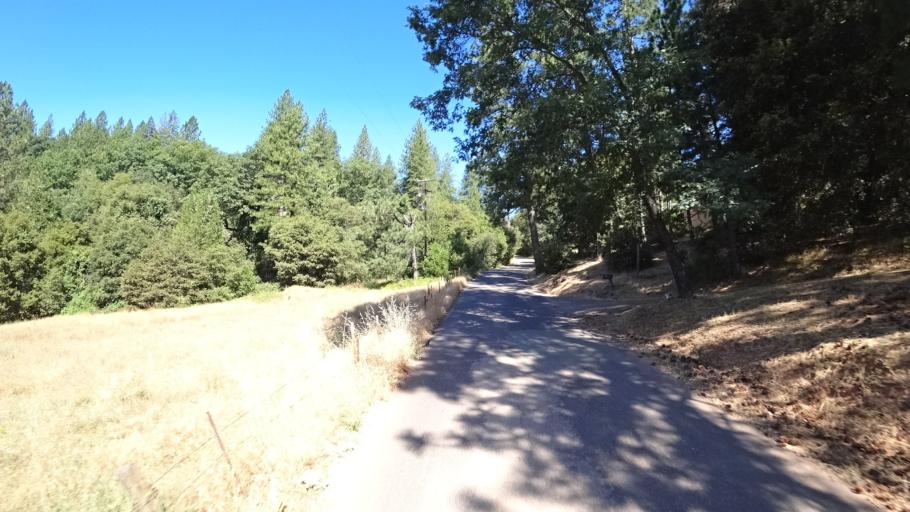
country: US
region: California
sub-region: Amador County
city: Pioneer
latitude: 38.3963
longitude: -120.4811
